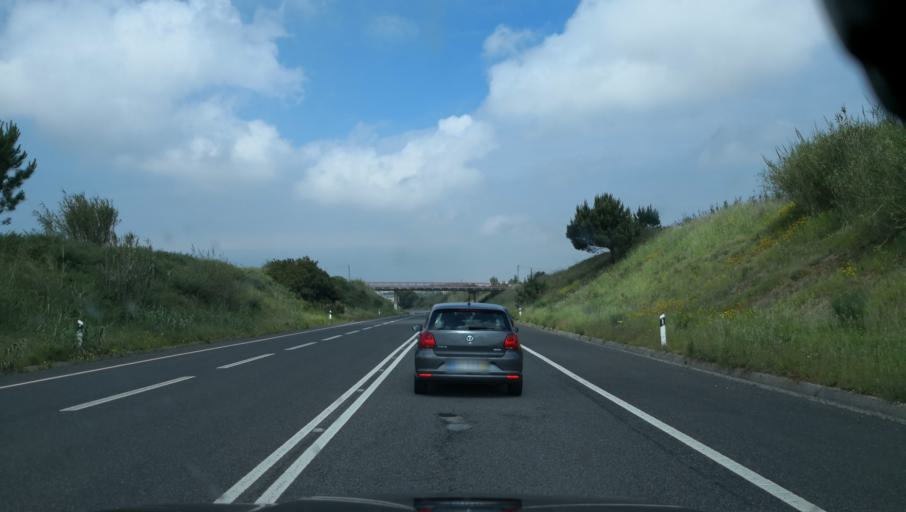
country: PT
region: Leiria
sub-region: Peniche
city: Atouguia da Baleia
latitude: 39.3257
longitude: -9.2837
